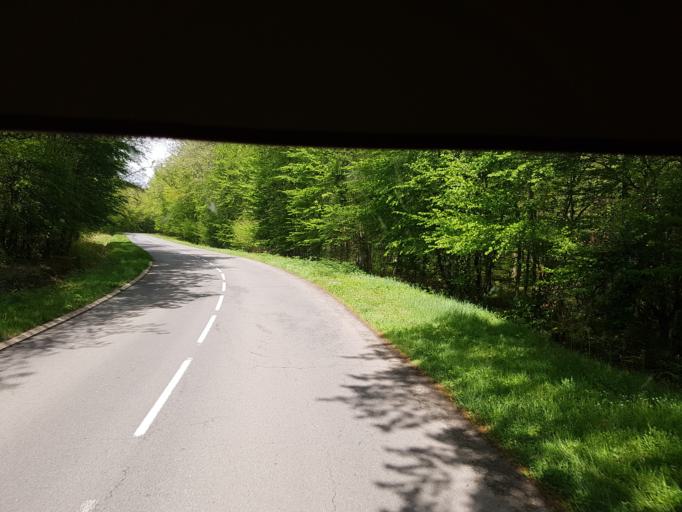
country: FR
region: Bourgogne
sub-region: Departement de Saone-et-Loire
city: Toulon-sur-Arroux
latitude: 46.6788
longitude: 4.1797
